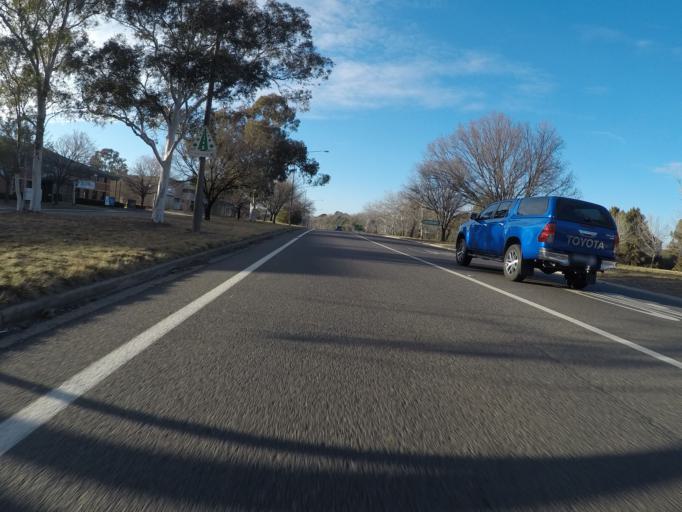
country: AU
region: Australian Capital Territory
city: Forrest
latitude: -35.3233
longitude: 149.1505
